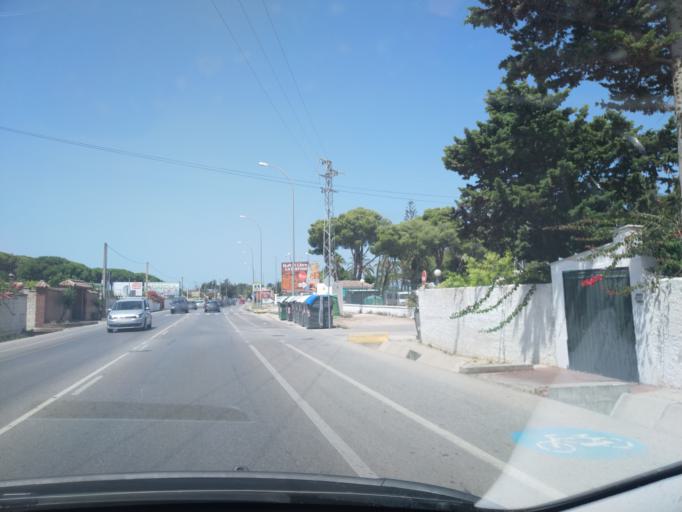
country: ES
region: Andalusia
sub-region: Provincia de Cadiz
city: Chiclana de la Frontera
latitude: 36.3944
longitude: -6.1558
